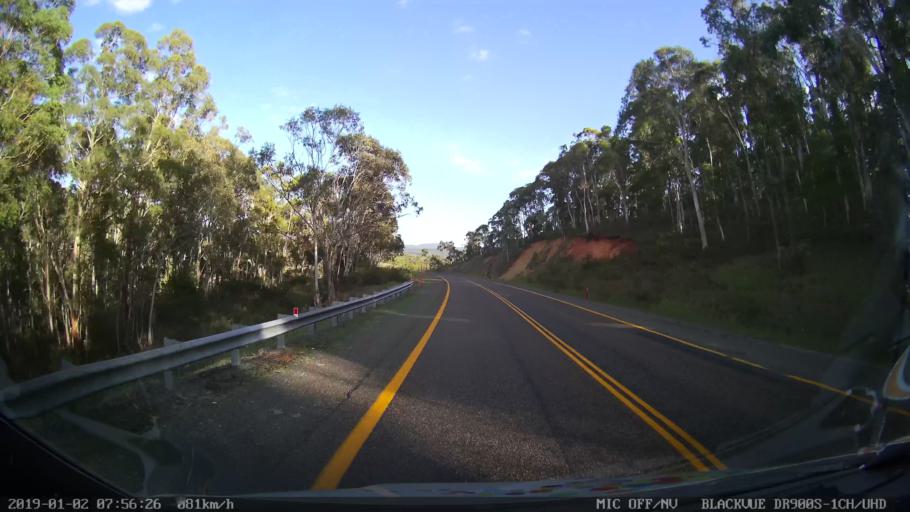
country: AU
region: New South Wales
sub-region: Tumut Shire
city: Tumut
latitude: -35.6707
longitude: 148.4852
